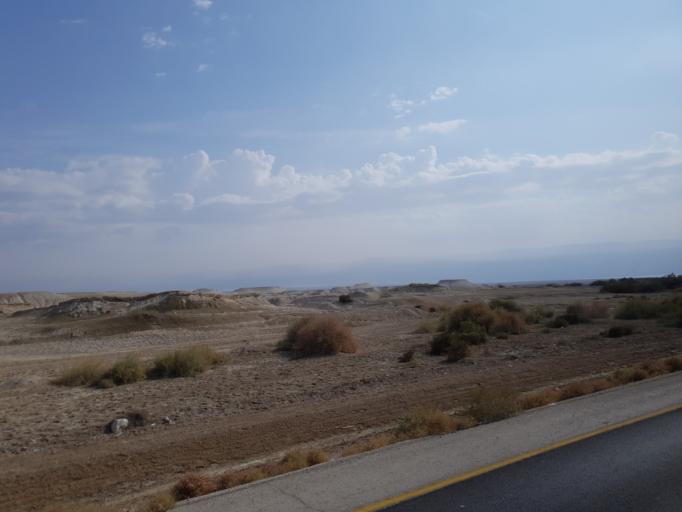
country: PS
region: West Bank
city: Jericho
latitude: 31.7936
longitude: 35.4969
